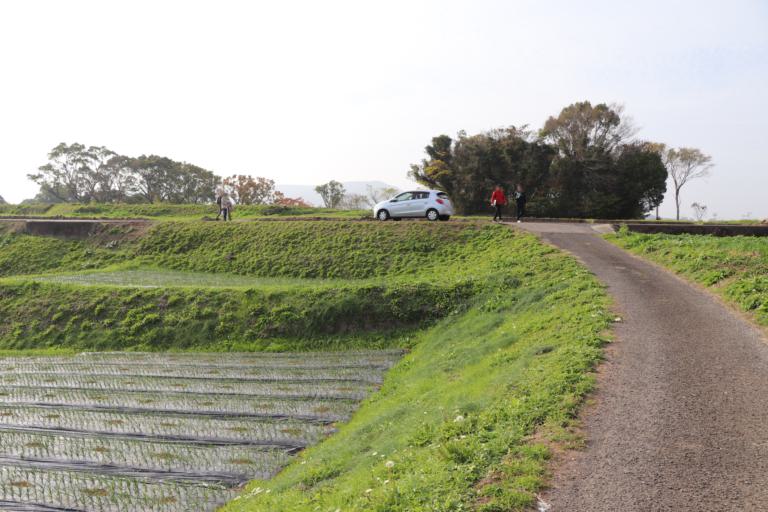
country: JP
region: Nagasaki
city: Shimabara
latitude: 32.6315
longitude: 130.2551
